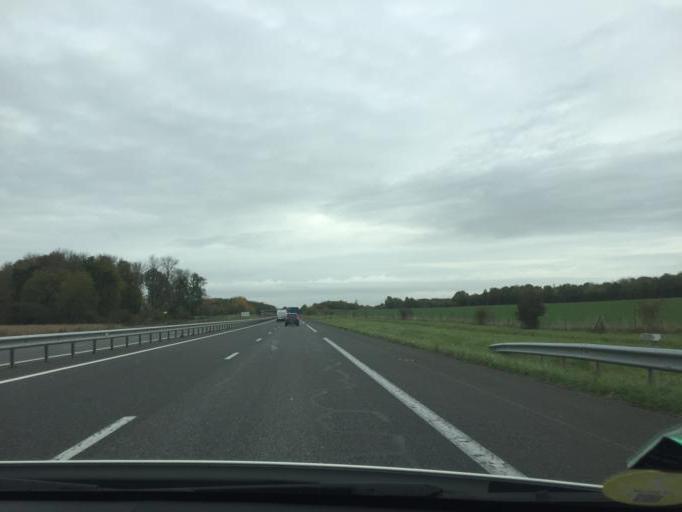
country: FR
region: Bourgogne
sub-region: Departement de l'Yonne
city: Egriselles-le-Bocage
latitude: 48.1391
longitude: 3.1568
